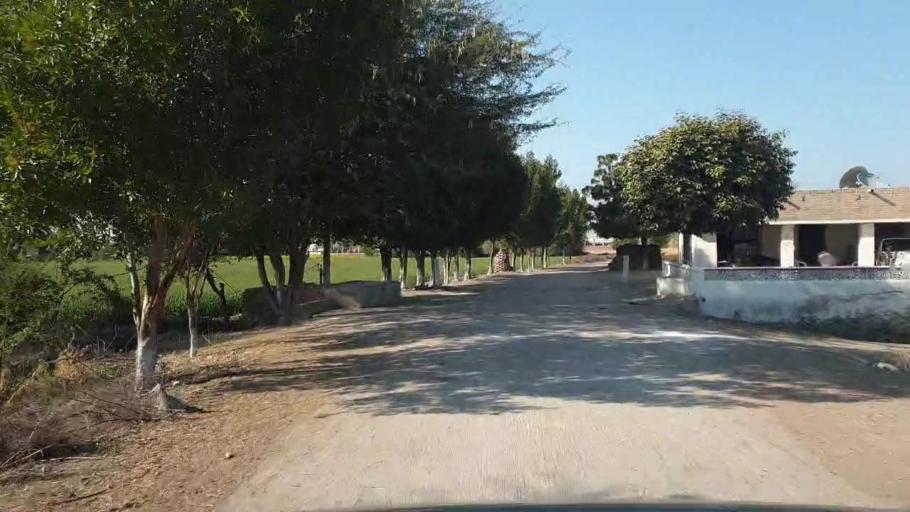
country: PK
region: Sindh
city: Shahpur Chakar
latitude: 26.1751
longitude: 68.6783
